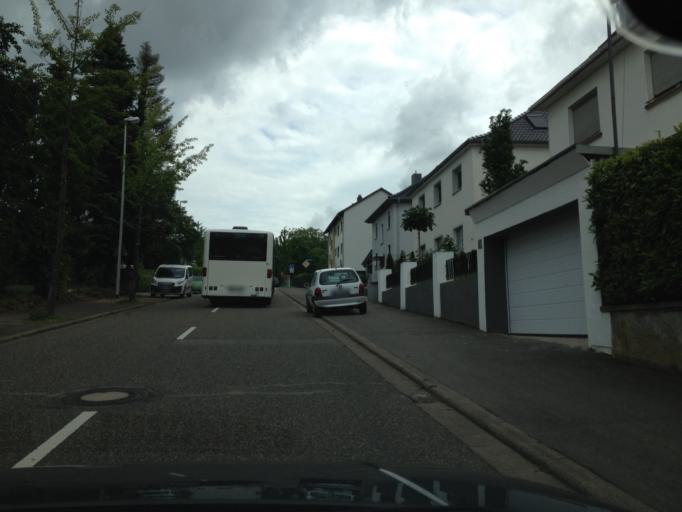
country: DE
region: Rheinland-Pfalz
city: Zweibrucken
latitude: 49.2489
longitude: 7.3820
